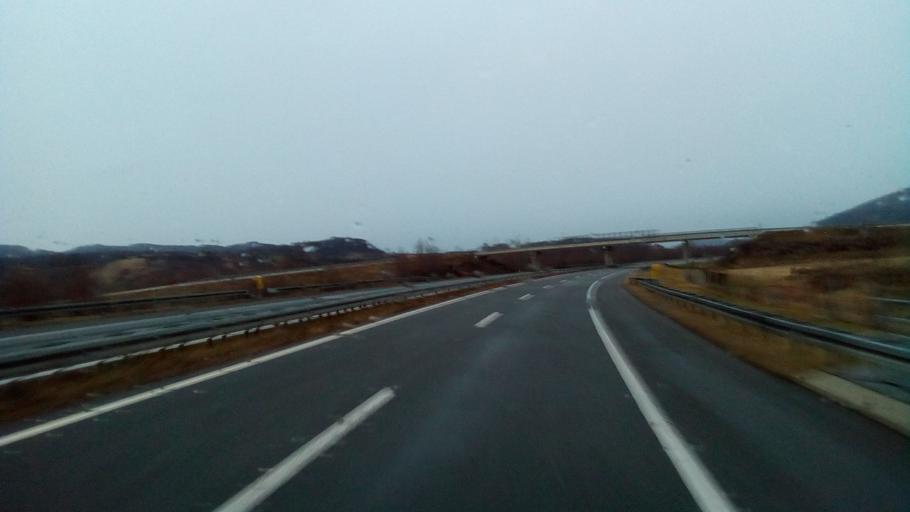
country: HR
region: Varazdinska
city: Ljubescica
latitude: 46.1777
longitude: 16.3785
